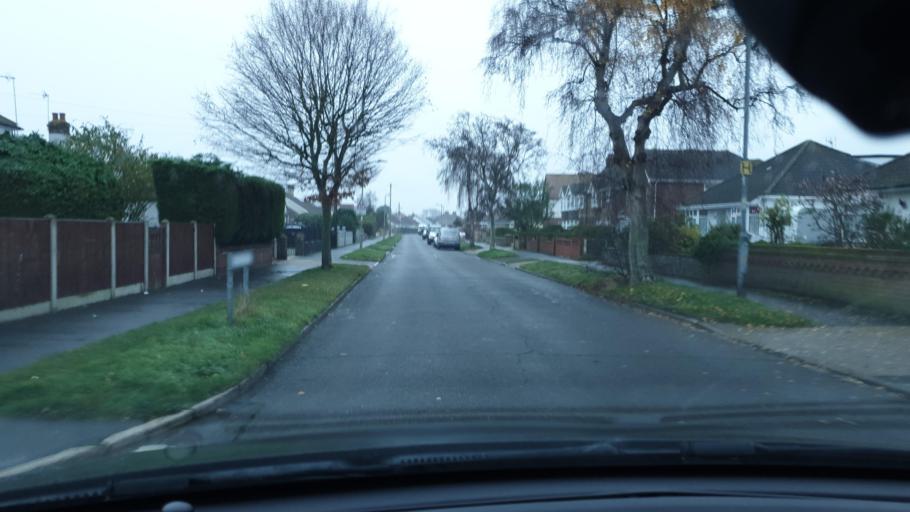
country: GB
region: England
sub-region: Essex
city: Clacton-on-Sea
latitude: 51.7982
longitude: 1.1393
